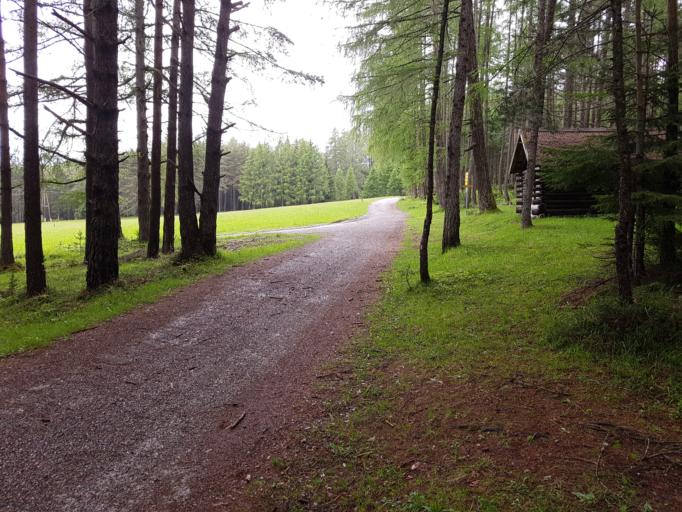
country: AT
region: Tyrol
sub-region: Politischer Bezirk Imst
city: Obsteig
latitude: 47.3082
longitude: 10.9107
